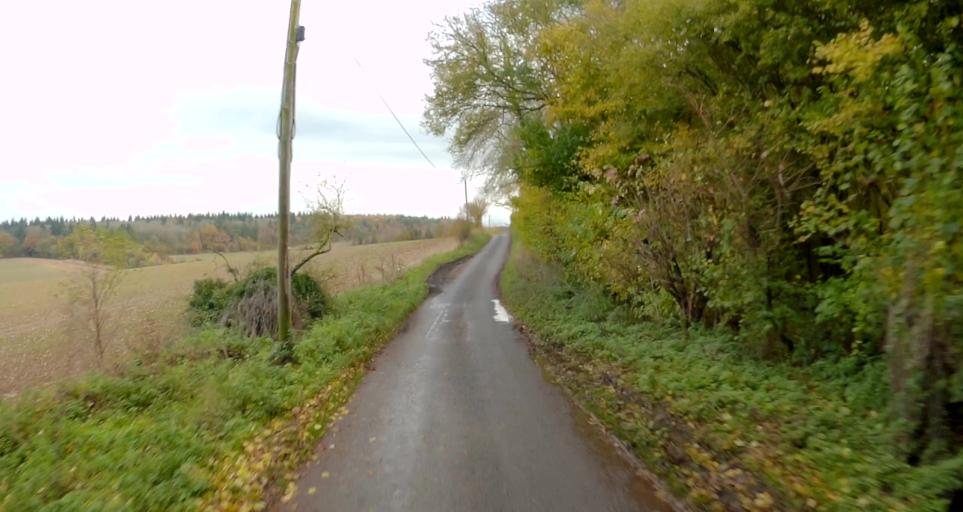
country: GB
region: England
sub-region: Hampshire
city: Long Sutton
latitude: 51.2136
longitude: -0.9605
